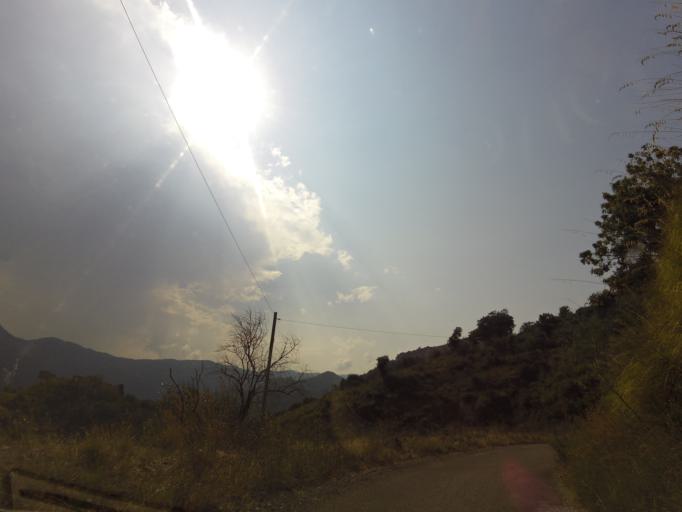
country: IT
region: Calabria
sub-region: Provincia di Reggio Calabria
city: Stilo
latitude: 38.4926
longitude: 16.4668
